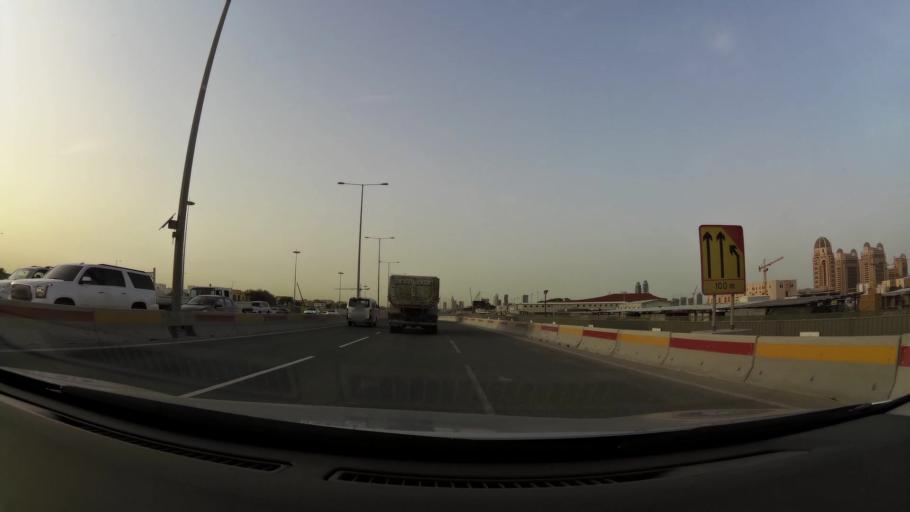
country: QA
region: Baladiyat ad Dawhah
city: Doha
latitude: 25.3456
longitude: 51.5211
